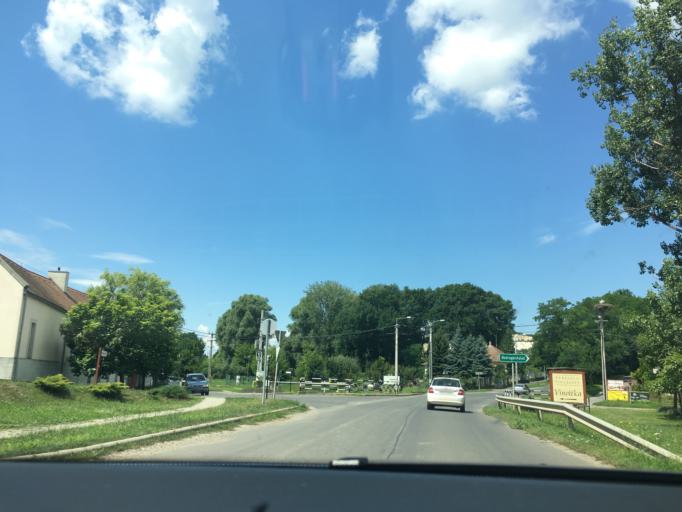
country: HU
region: Borsod-Abauj-Zemplen
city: Tarcal
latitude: 48.1695
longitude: 21.3621
